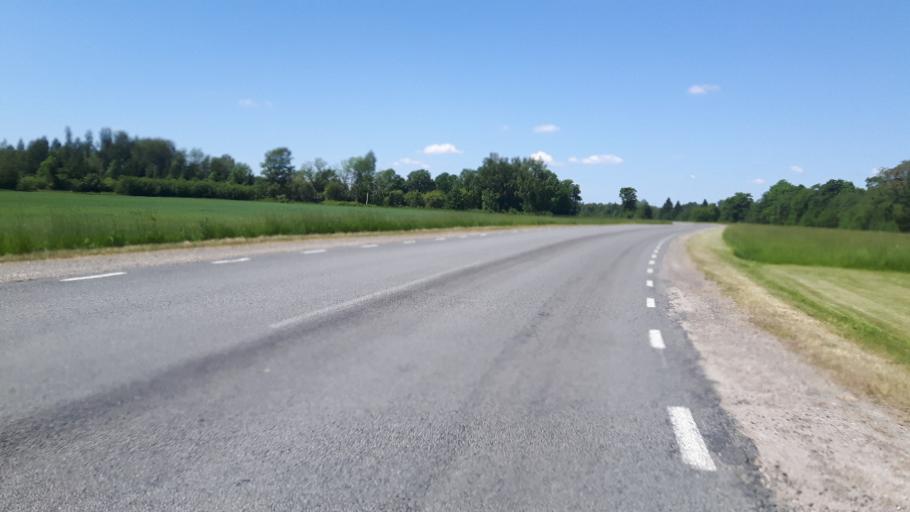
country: EE
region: Paernumaa
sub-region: Tootsi vald
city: Tootsi
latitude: 58.4946
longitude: 24.8880
